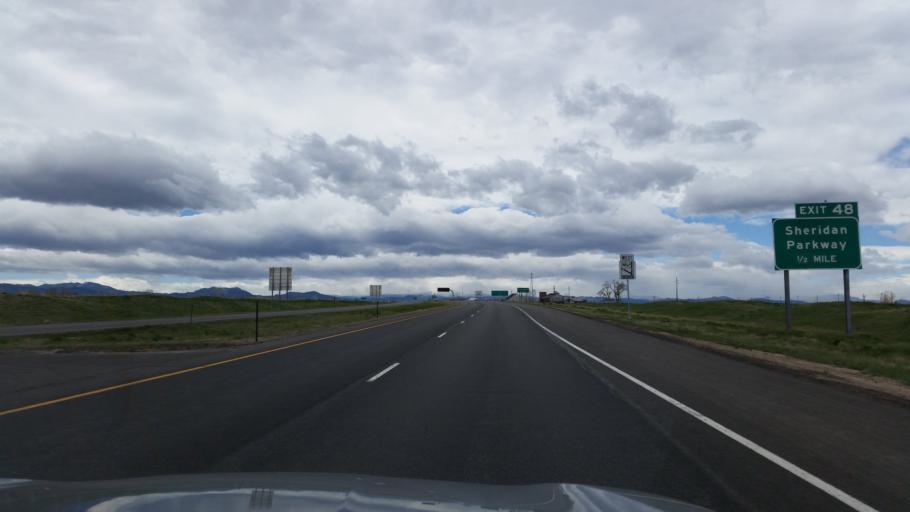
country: US
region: Colorado
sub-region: Boulder County
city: Erie
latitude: 39.9841
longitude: -105.0001
